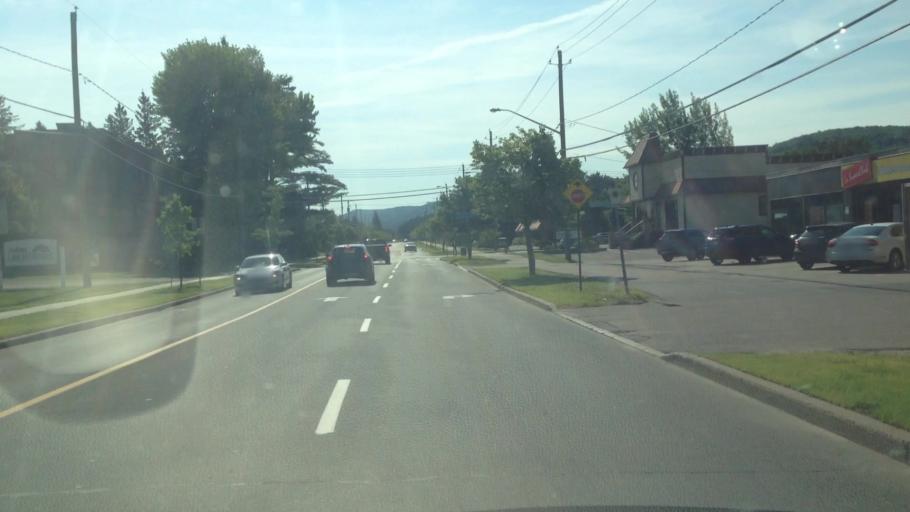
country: CA
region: Quebec
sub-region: Laurentides
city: Mont-Tremblant
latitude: 46.1192
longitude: -74.5726
